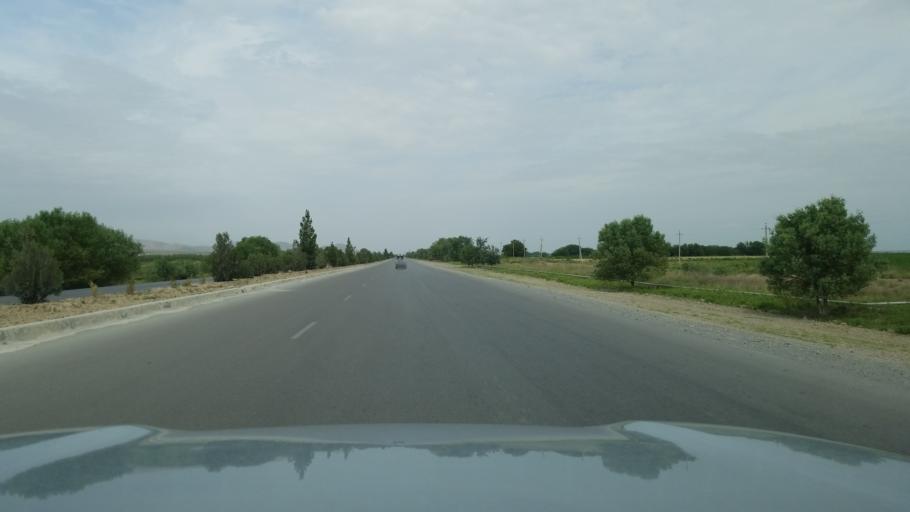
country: TM
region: Ahal
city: Arcabil
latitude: 38.1879
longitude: 57.8498
